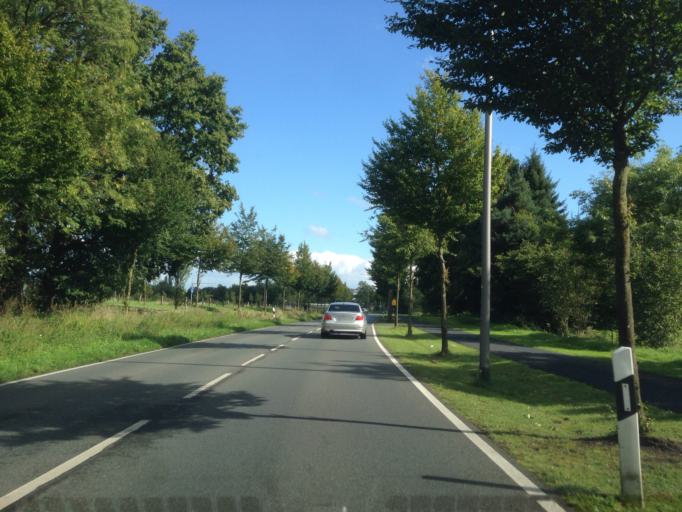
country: DE
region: North Rhine-Westphalia
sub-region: Regierungsbezirk Munster
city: Muenster
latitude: 51.9713
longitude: 7.5844
